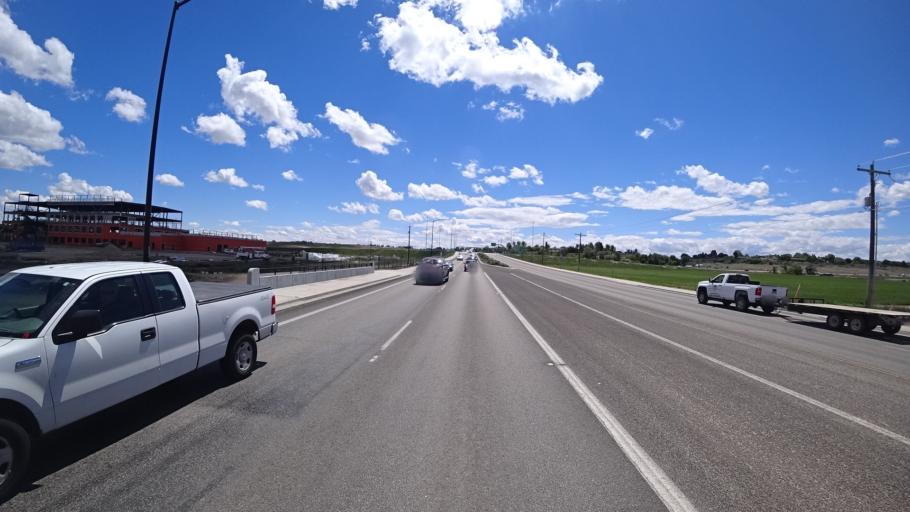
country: US
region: Idaho
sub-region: Ada County
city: Meridian
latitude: 43.5976
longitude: -116.4339
